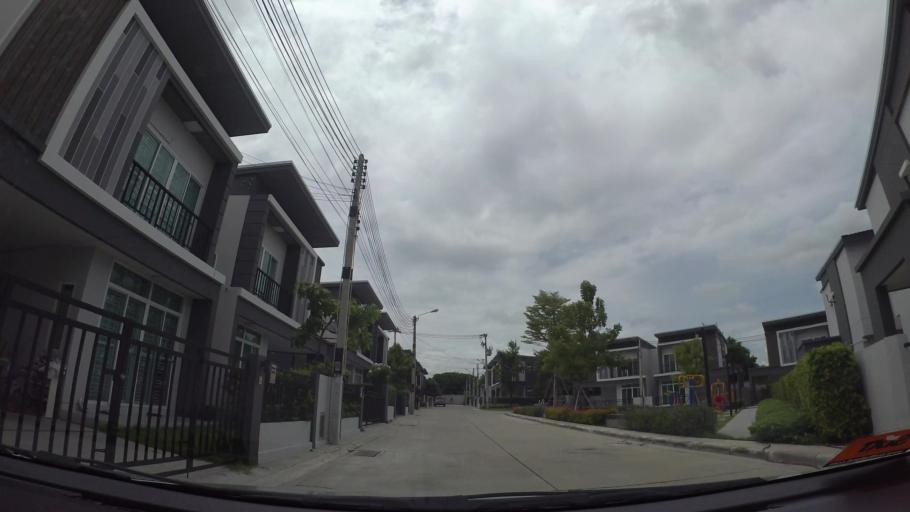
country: TH
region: Chon Buri
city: Si Racha
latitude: 13.1601
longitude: 100.9790
